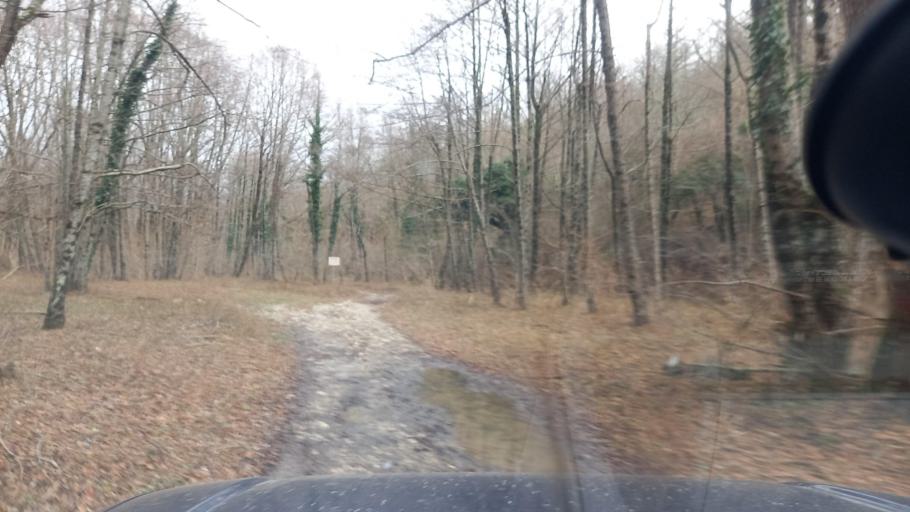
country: RU
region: Krasnodarskiy
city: Pshada
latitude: 44.4863
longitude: 38.4115
